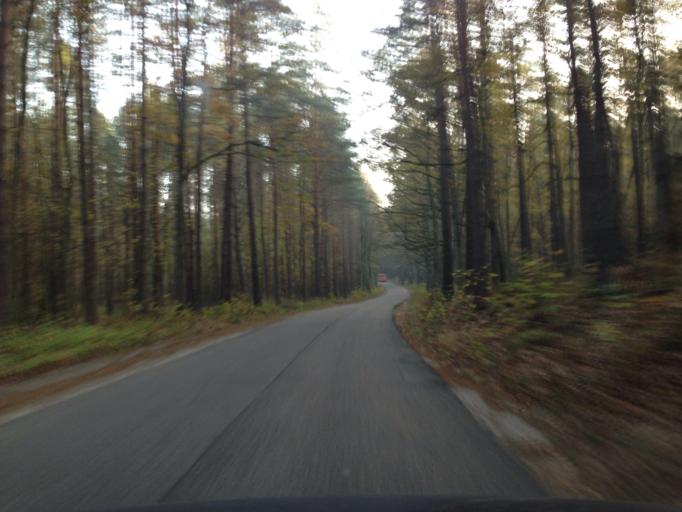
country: PL
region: Warmian-Masurian Voivodeship
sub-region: Powiat dzialdowski
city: Lidzbark
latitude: 53.2504
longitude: 19.7445
